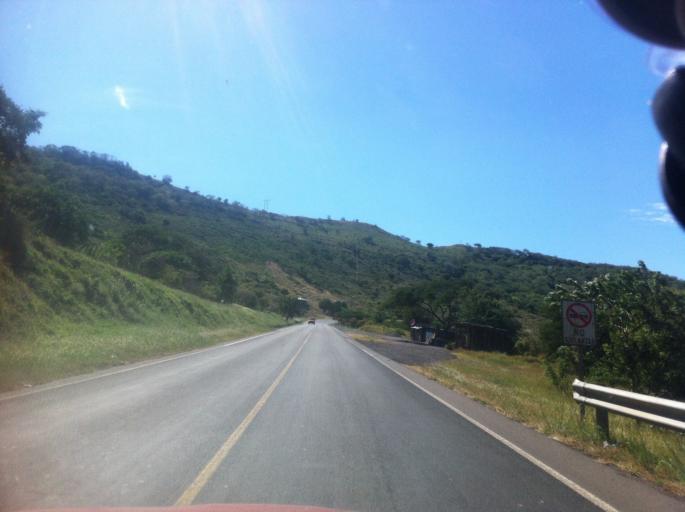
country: NI
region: Boaco
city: Teustepe
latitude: 12.3536
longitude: -85.9134
